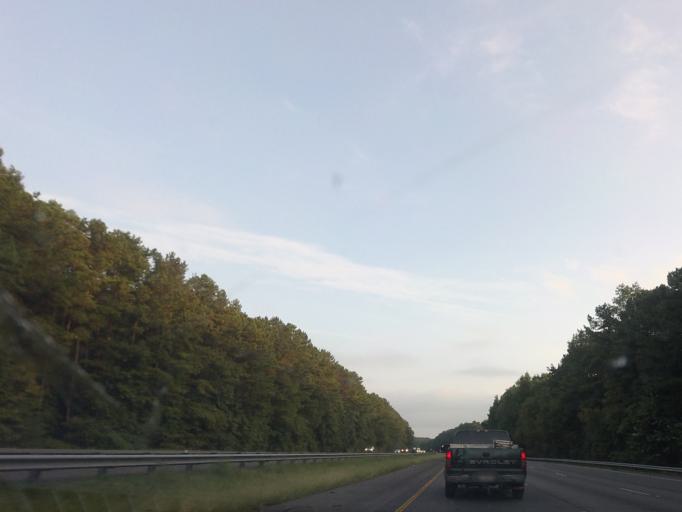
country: US
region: Georgia
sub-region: Butts County
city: Indian Springs
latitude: 33.1717
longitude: -84.0430
